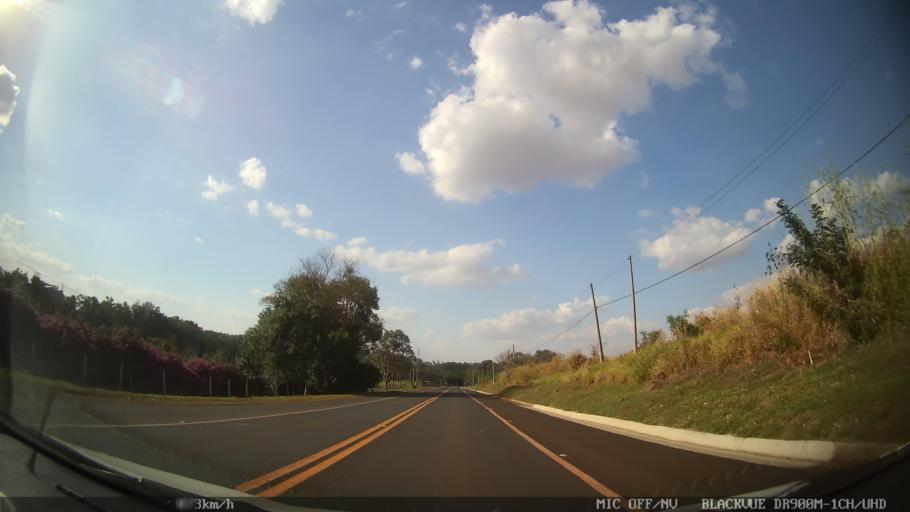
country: BR
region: Sao Paulo
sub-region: Ribeirao Preto
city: Ribeirao Preto
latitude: -21.1787
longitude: -47.8551
